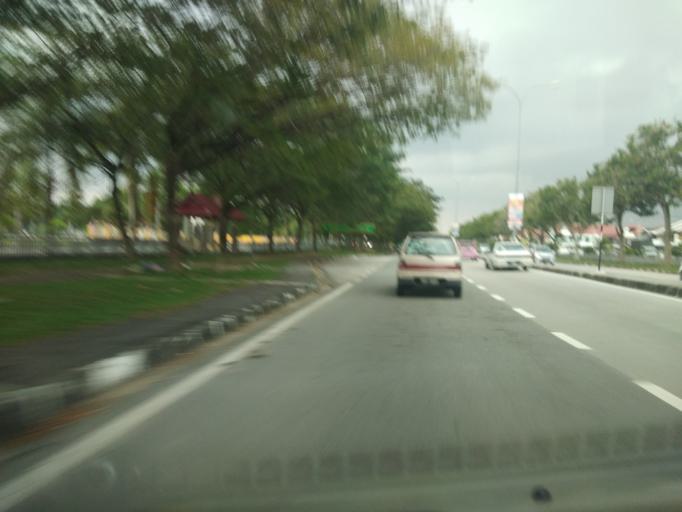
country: MY
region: Penang
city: Kepala Batas
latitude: 5.5195
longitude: 100.4725
